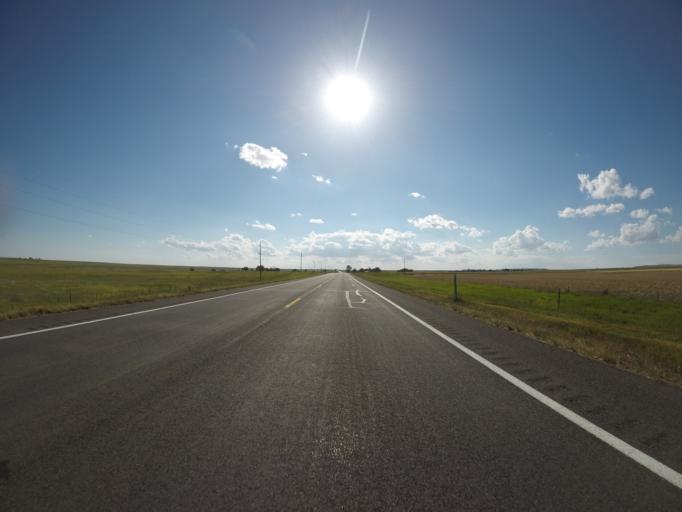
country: US
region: Colorado
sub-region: Morgan County
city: Fort Morgan
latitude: 40.6112
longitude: -103.7896
